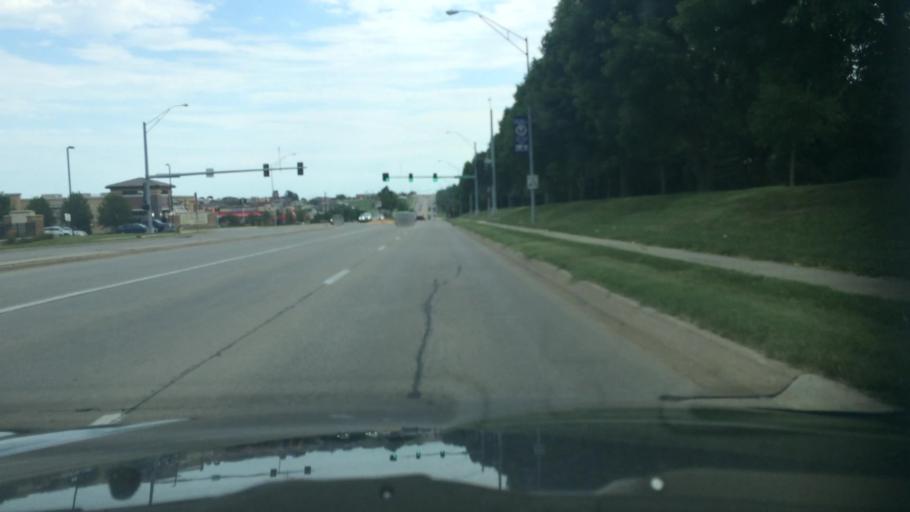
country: US
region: Nebraska
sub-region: Sarpy County
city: La Vista
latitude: 41.1739
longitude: -96.0238
